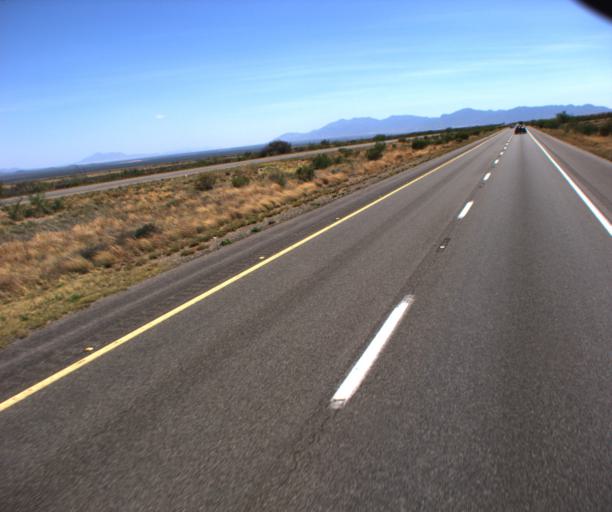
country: US
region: Arizona
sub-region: Cochise County
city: Whetstone
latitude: 31.8240
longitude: -110.3461
